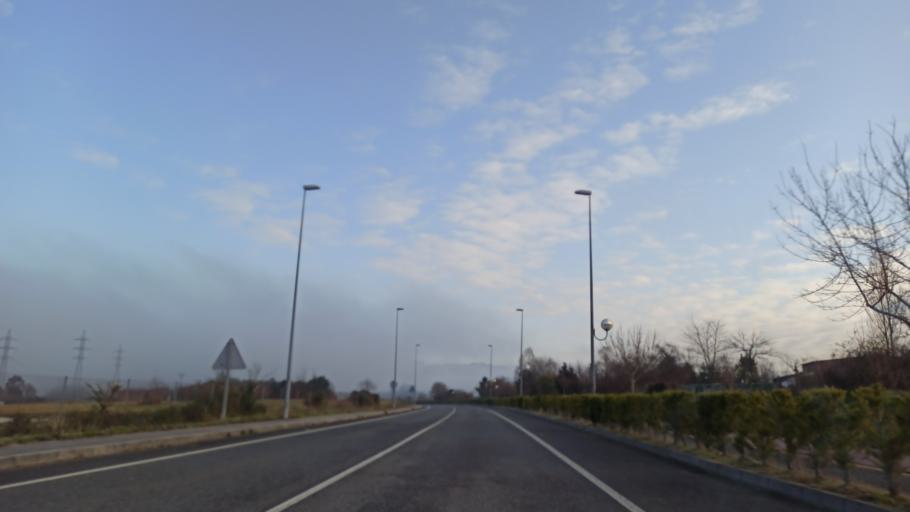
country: ES
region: Galicia
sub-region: Provincia da Coruna
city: As Pontes de Garcia Rodriguez
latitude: 43.4543
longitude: -7.8663
